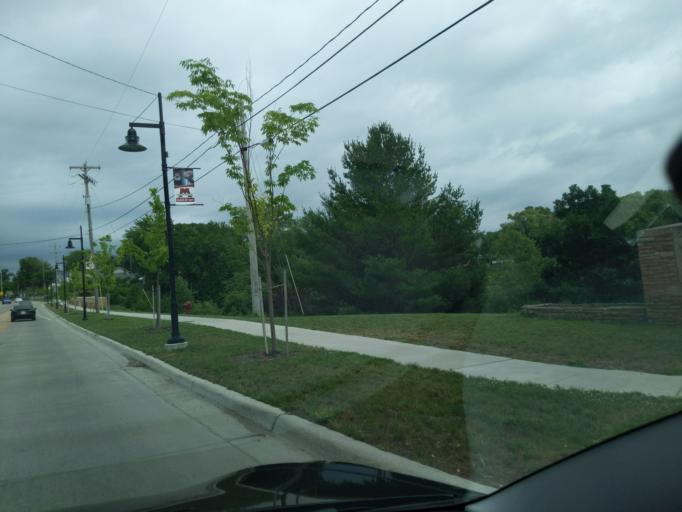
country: US
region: Michigan
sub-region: Muskegon County
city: Roosevelt Park
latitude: 43.2178
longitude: -86.2857
